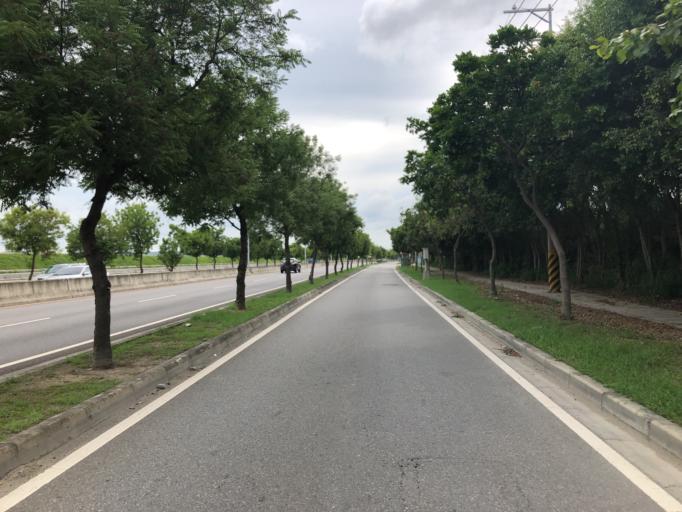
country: TW
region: Taiwan
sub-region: Taichung City
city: Taichung
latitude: 24.0837
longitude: 120.6696
